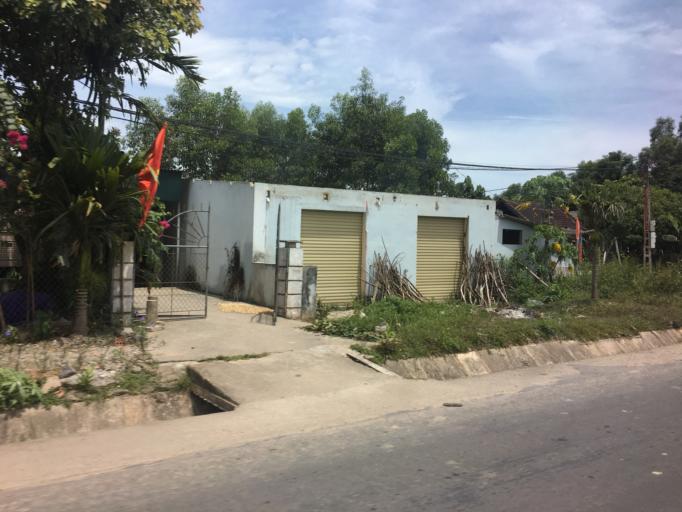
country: VN
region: Ha Tinh
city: Huong Khe
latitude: 18.2519
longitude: 105.6543
